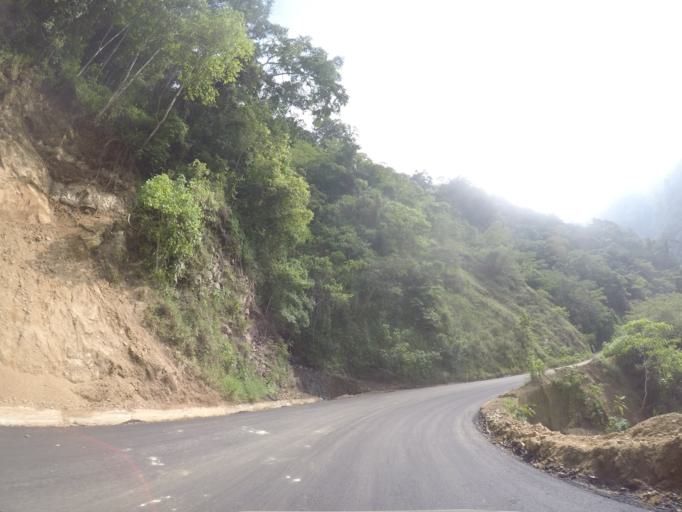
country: MX
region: Oaxaca
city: Pluma Hidalgo
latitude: 15.9397
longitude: -96.4339
